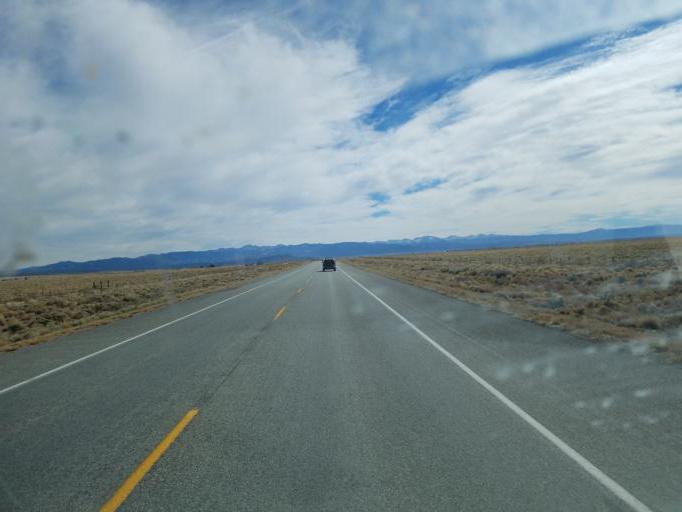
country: US
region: Colorado
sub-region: Alamosa County
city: Alamosa East
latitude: 37.4688
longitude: -105.5738
